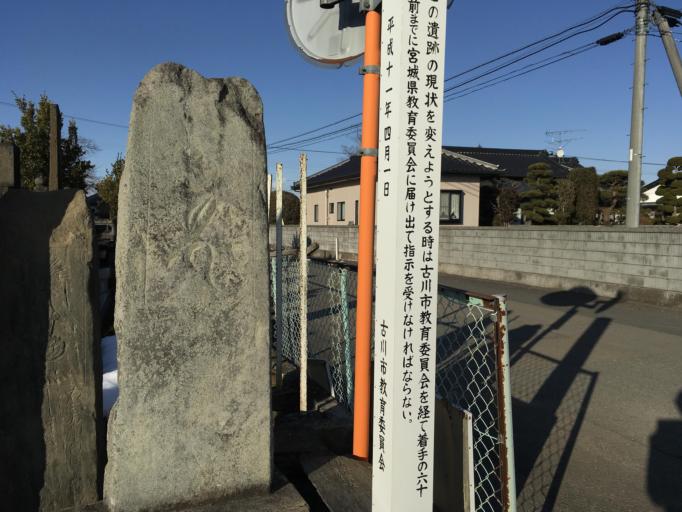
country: JP
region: Miyagi
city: Furukawa
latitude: 38.5342
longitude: 140.9013
